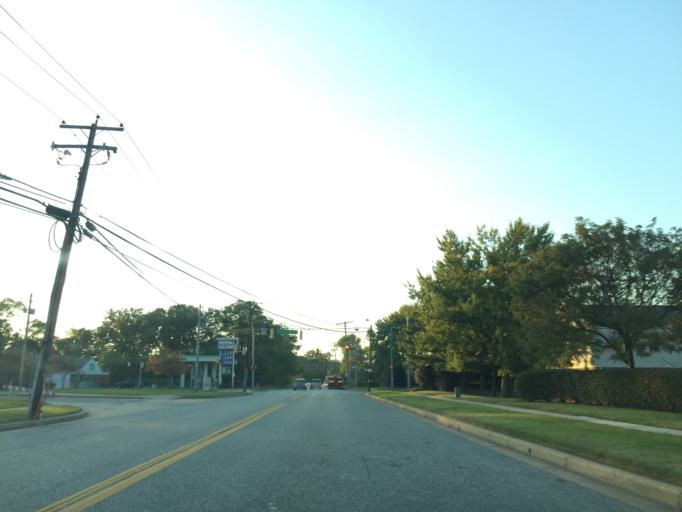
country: US
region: Maryland
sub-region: Baltimore County
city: Essex
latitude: 39.2949
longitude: -76.4567
